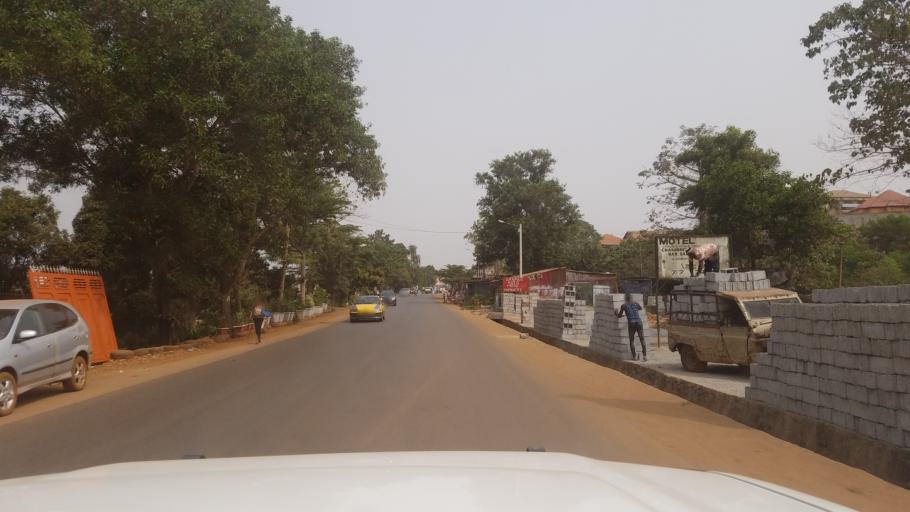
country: GN
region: Conakry
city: Conakry
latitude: 9.6482
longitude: -13.6025
